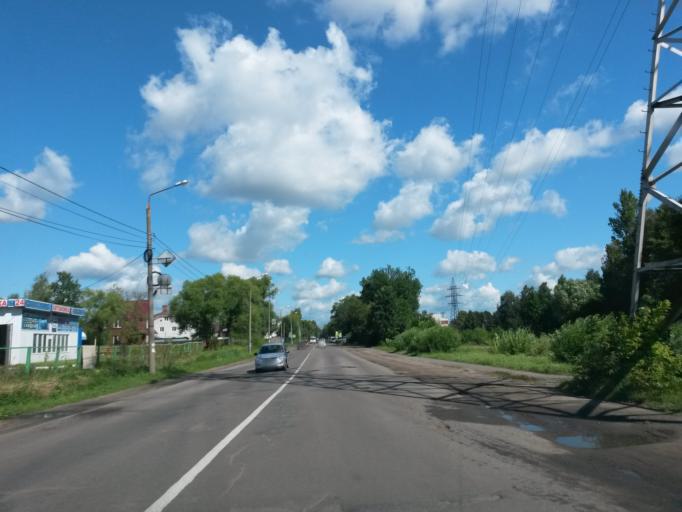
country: RU
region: Jaroslavl
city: Yaroslavl
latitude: 57.5873
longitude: 39.8764
